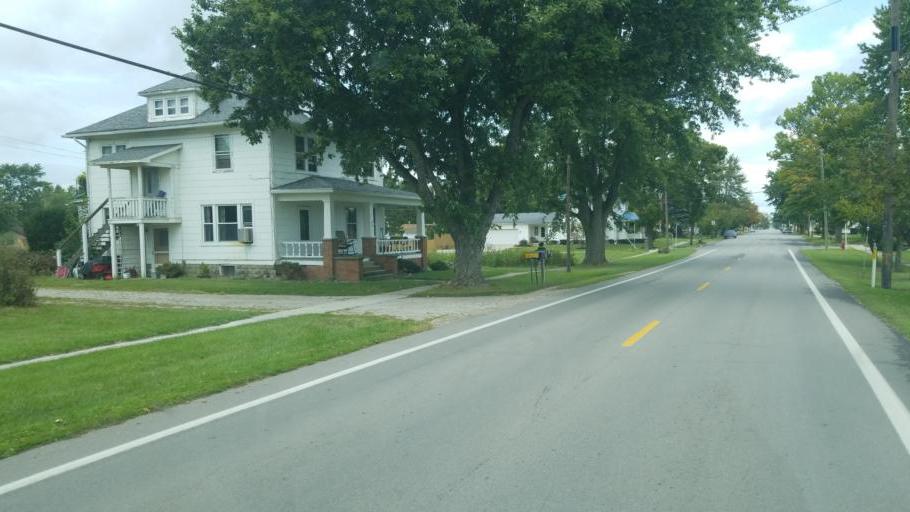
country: US
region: Ohio
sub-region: Seneca County
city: Tiffin
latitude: 41.0481
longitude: -83.0154
